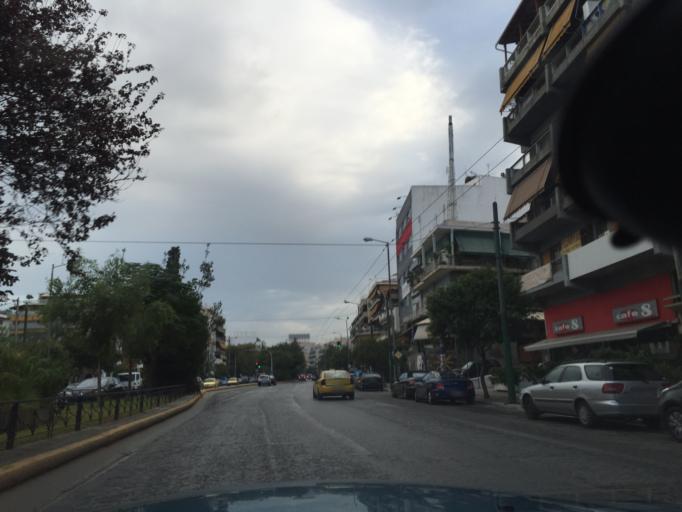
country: GR
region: Attica
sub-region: Nomarchia Athinas
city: Kallithea
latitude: 37.9515
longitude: 23.6940
